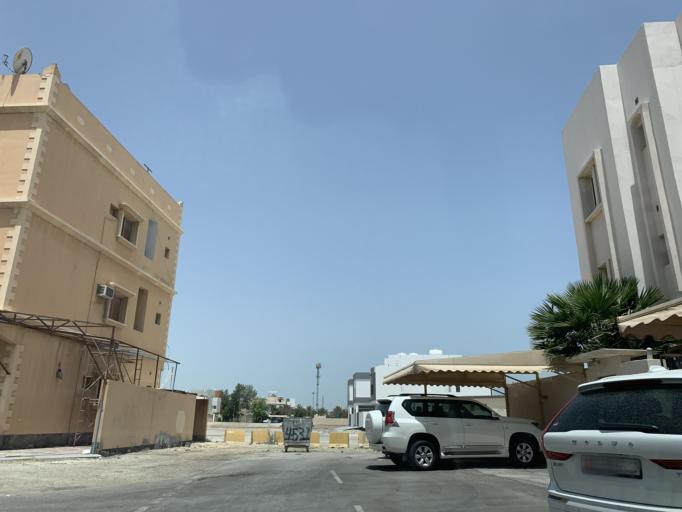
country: BH
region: Northern
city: Sitrah
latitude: 26.1429
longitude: 50.5908
